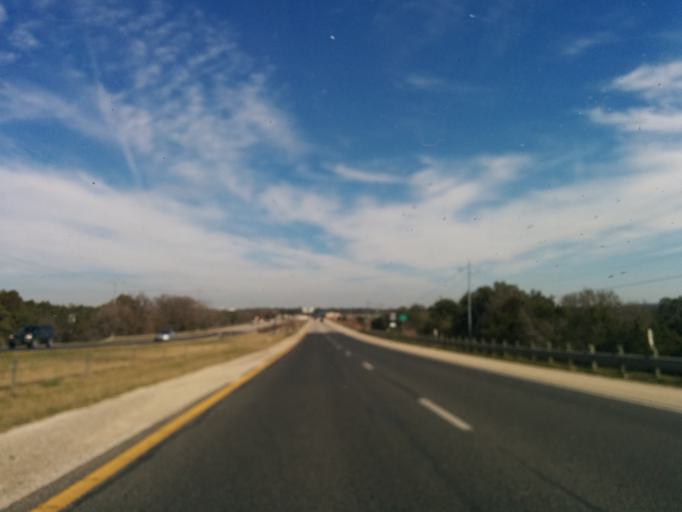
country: US
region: Texas
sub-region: Comal County
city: Bulverde
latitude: 29.7177
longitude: -98.4447
